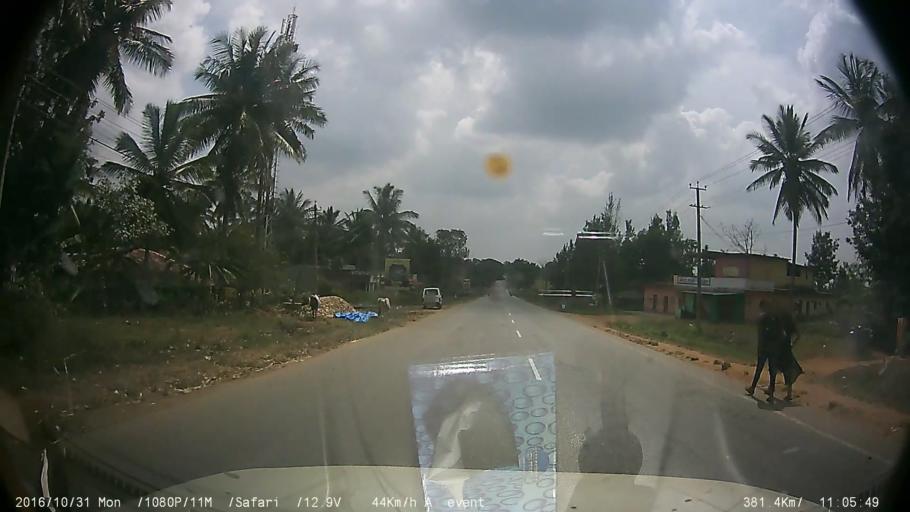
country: IN
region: Karnataka
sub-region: Mysore
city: Piriyapatna
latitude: 12.3782
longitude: 76.0372
